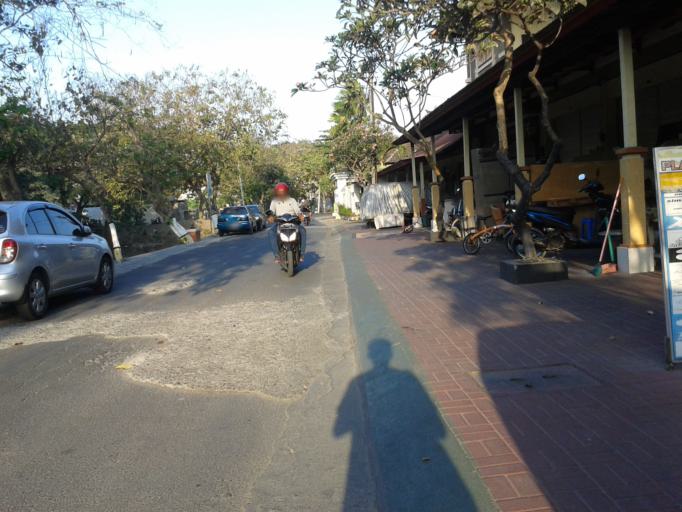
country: ID
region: Bali
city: Kuta
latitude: -8.7046
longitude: 115.1743
